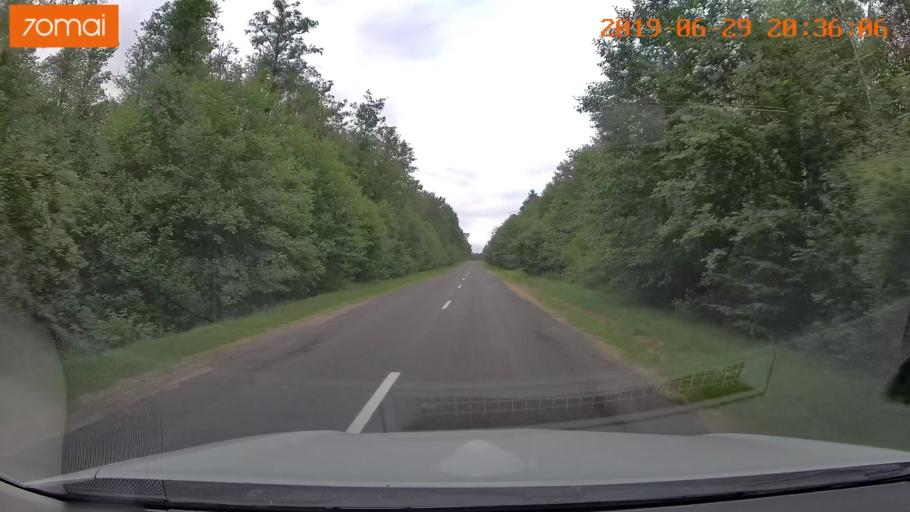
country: BY
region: Brest
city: Hantsavichy
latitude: 52.5225
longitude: 26.3558
